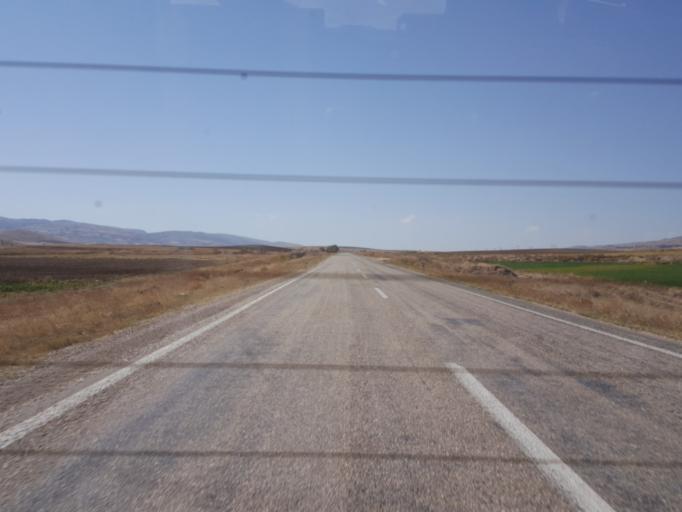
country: TR
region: Amasya
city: Dogantepe
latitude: 40.5756
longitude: 35.5985
